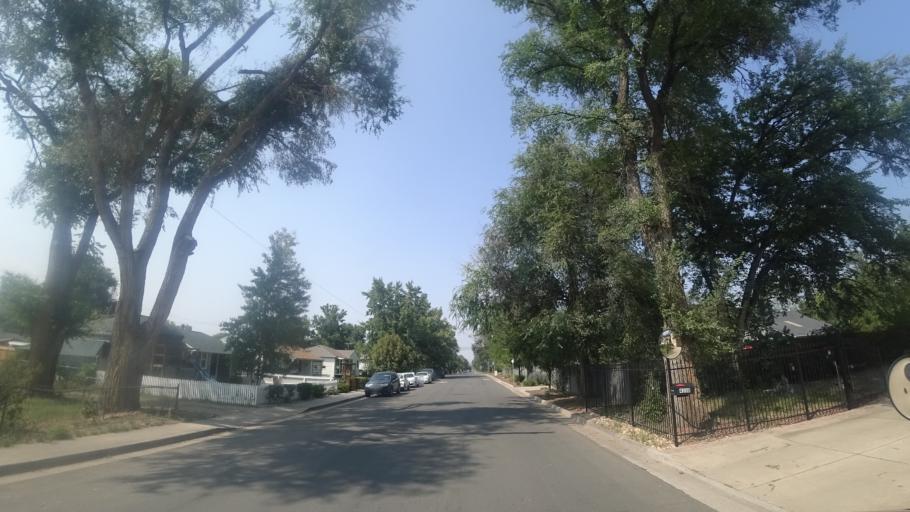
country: US
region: Colorado
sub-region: Arapahoe County
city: Englewood
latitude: 39.6377
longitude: -104.9785
